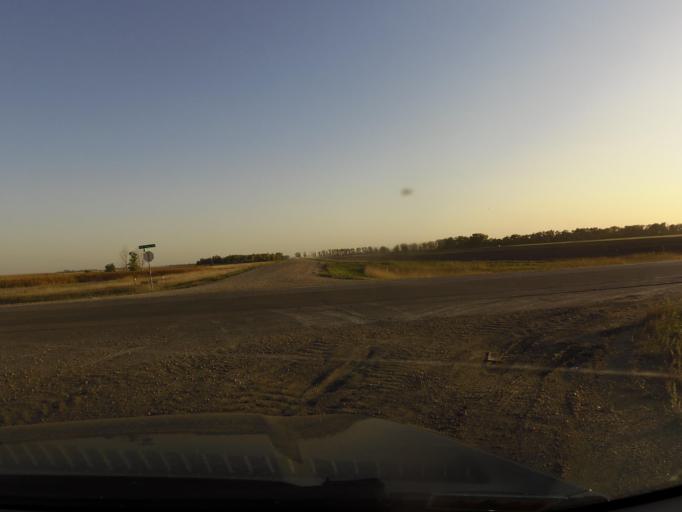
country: US
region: North Dakota
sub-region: Walsh County
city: Grafton
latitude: 48.4129
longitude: -97.4702
